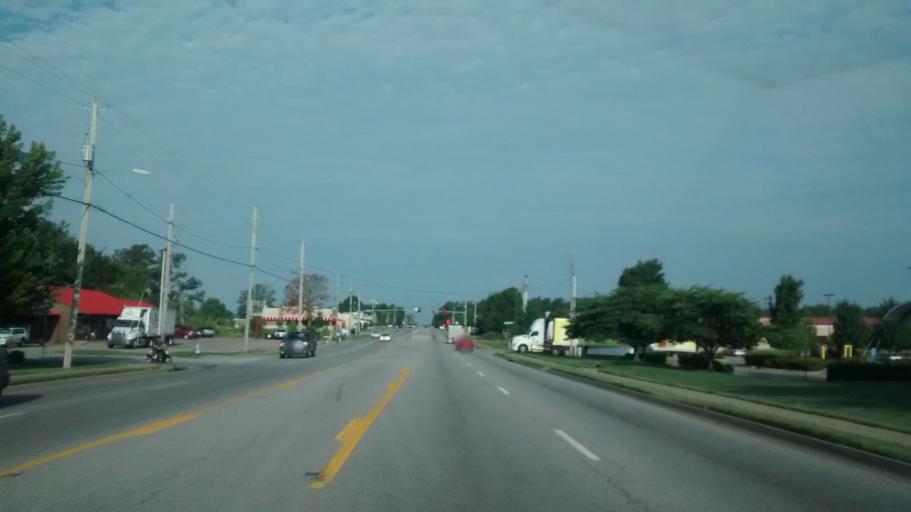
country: US
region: Arkansas
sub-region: Washington County
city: Fayetteville
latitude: 36.0785
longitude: -94.2054
